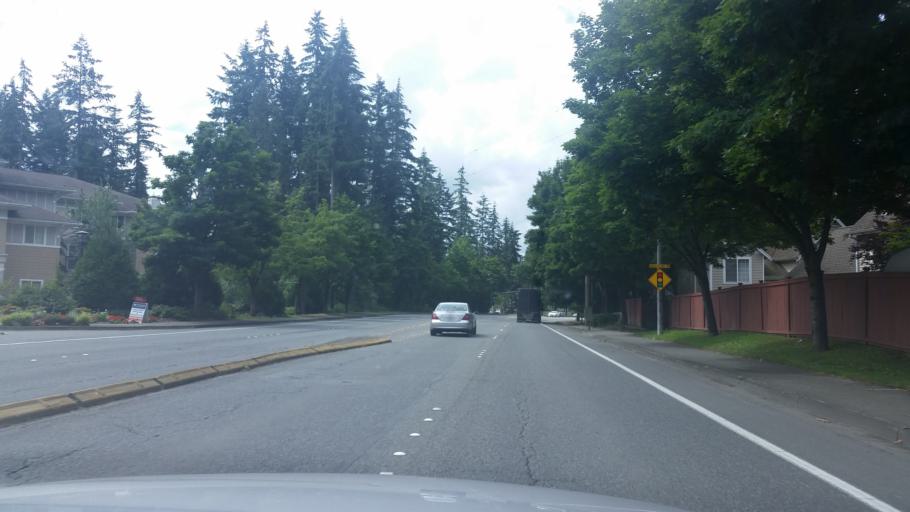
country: US
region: Washington
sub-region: King County
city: Redmond
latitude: 47.6891
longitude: -122.0922
